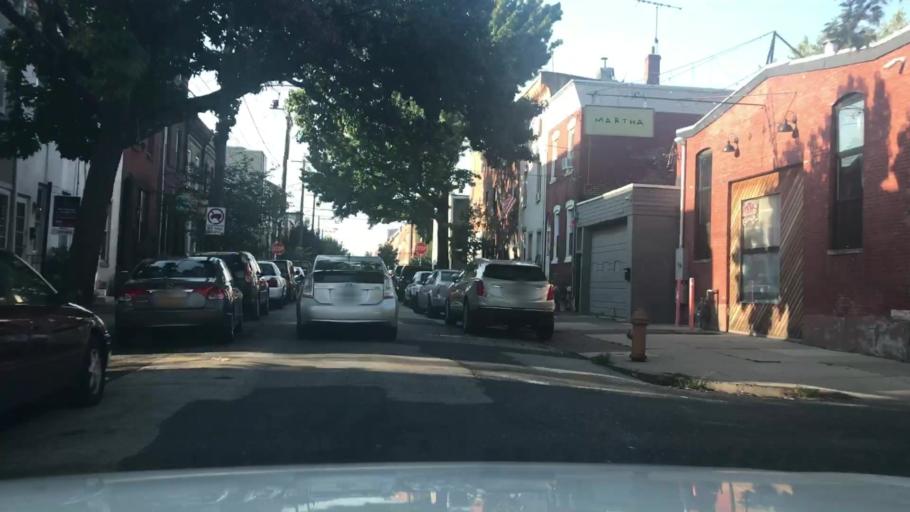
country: US
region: Pennsylvania
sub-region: Philadelphia County
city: Philadelphia
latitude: 39.9820
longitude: -75.1282
